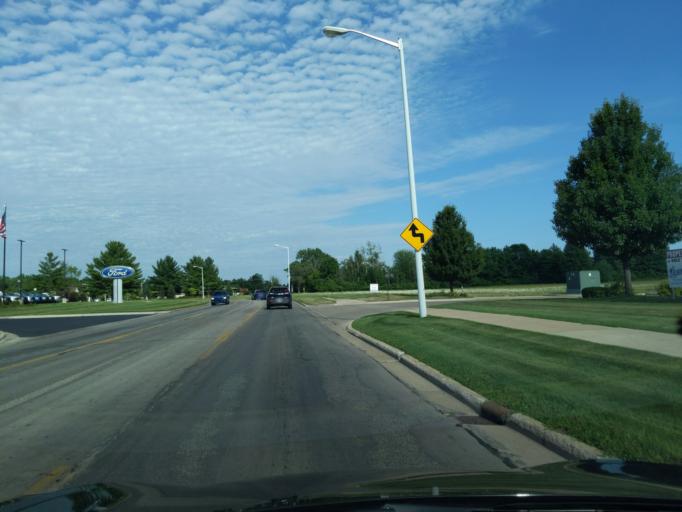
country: US
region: Michigan
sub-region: Midland County
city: Midland
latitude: 43.6584
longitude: -84.2318
